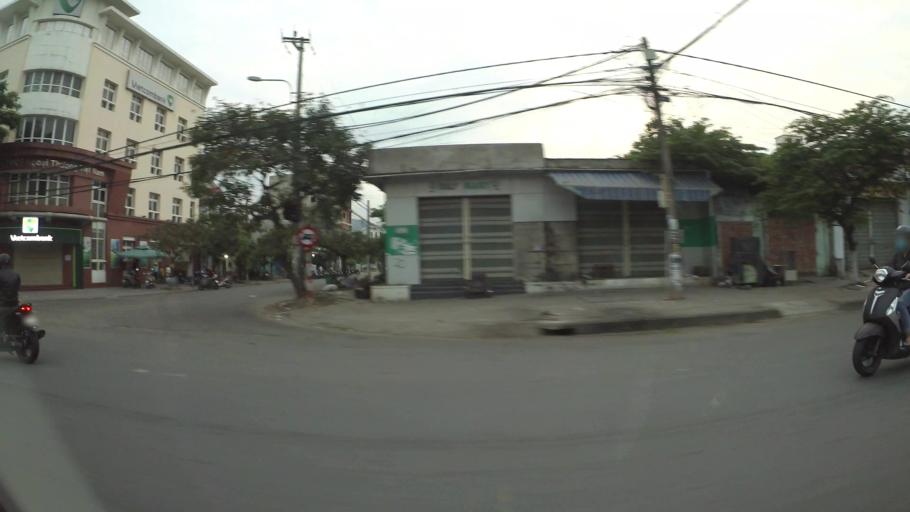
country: VN
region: Da Nang
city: Lien Chieu
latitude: 16.0811
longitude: 108.1467
